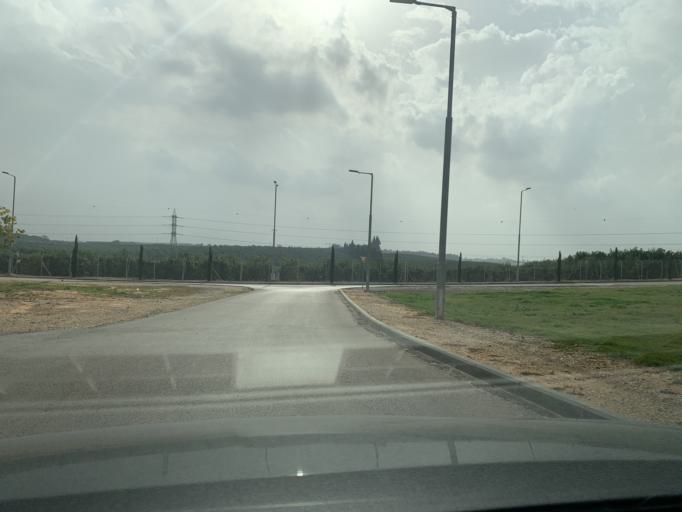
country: IL
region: Central District
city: Tirah
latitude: 32.2154
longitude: 34.9351
